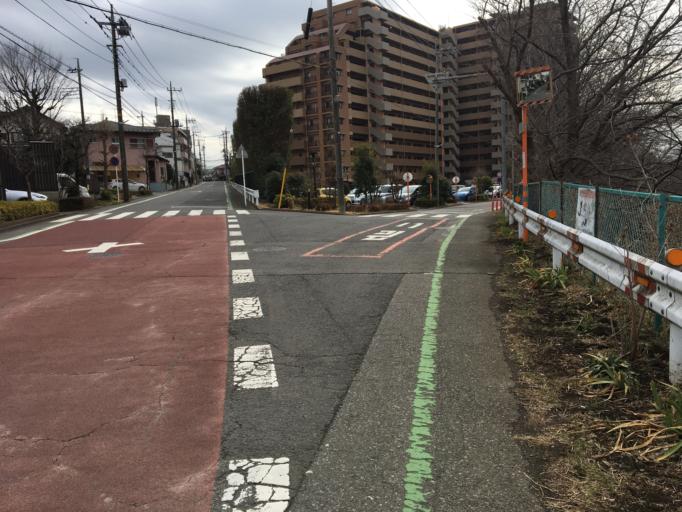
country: JP
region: Saitama
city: Tokorozawa
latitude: 35.8036
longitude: 139.5132
